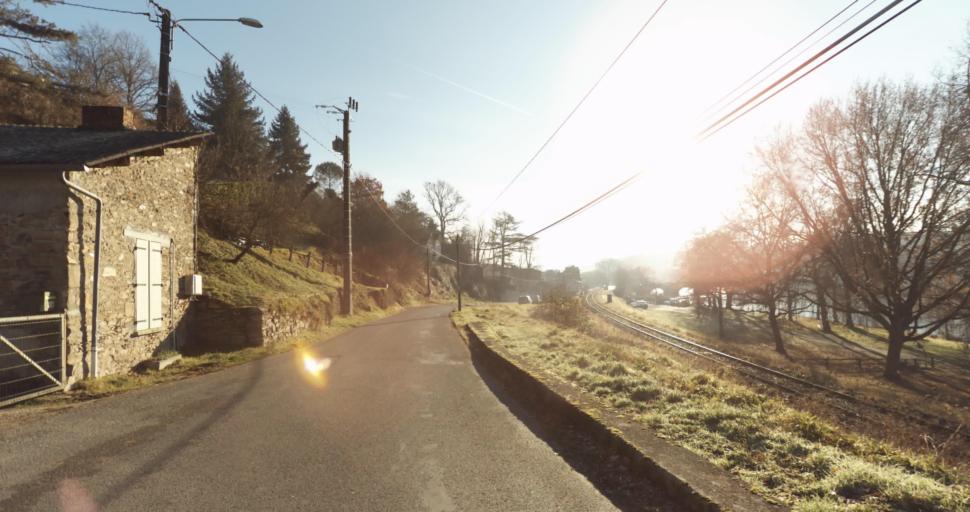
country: FR
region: Limousin
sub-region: Departement de la Haute-Vienne
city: Aixe-sur-Vienne
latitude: 45.7996
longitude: 1.1413
